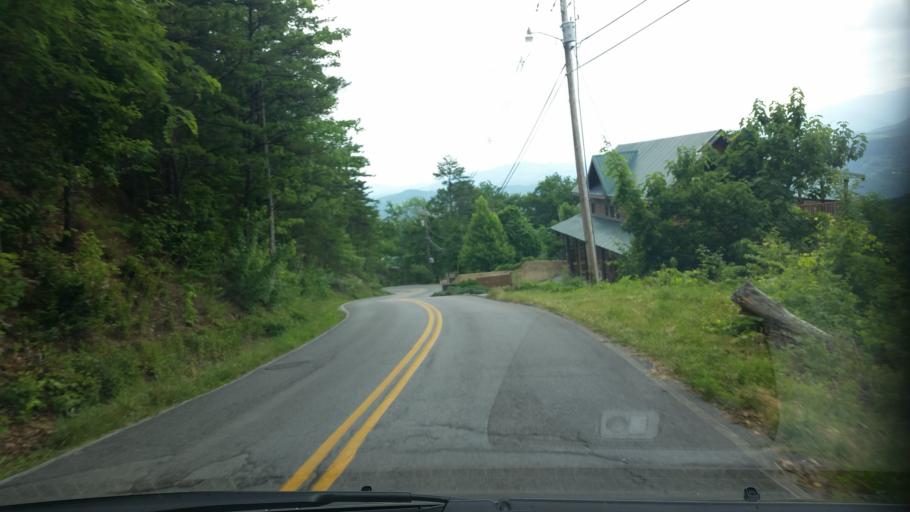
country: US
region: Tennessee
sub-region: Sevier County
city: Gatlinburg
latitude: 35.7085
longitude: -83.5579
